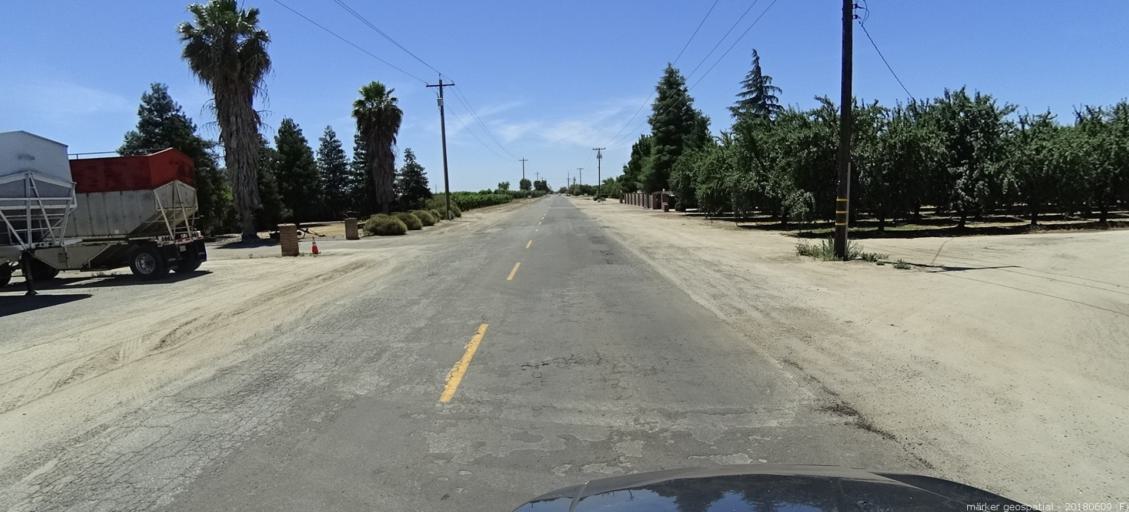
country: US
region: California
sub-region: Madera County
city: Parkwood
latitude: 36.9277
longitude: -120.0652
